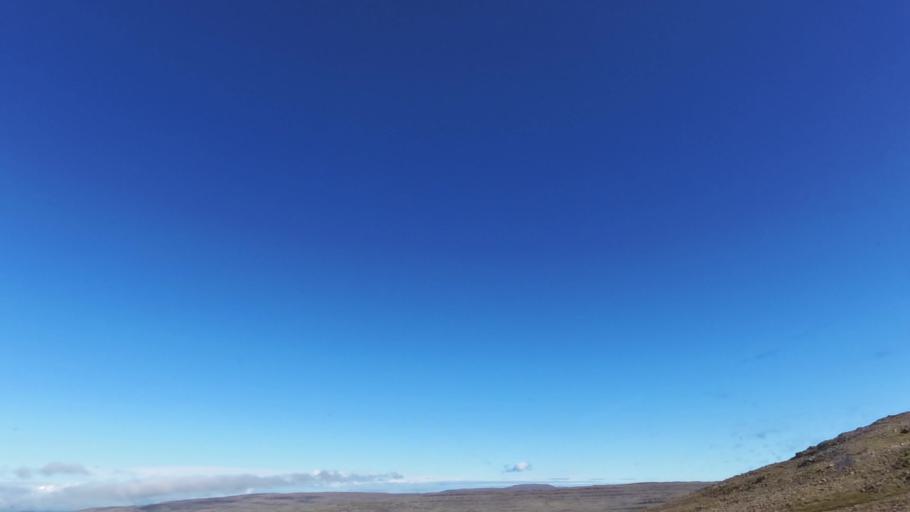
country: IS
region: West
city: Olafsvik
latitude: 65.5561
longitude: -24.2312
